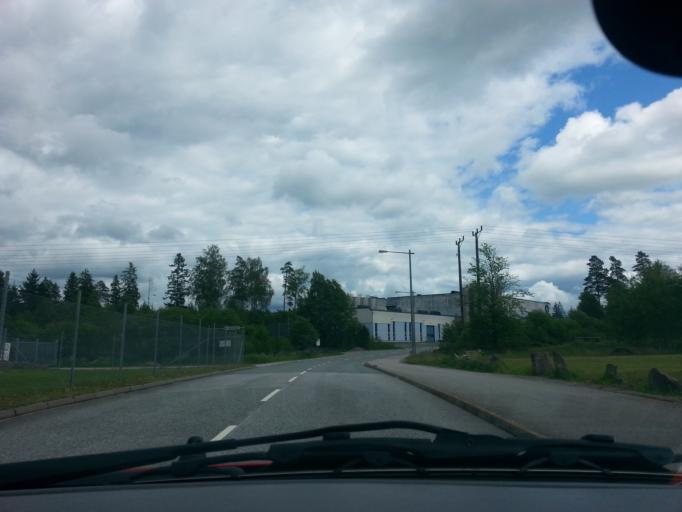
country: SE
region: Joenkoeping
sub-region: Gislaveds Kommun
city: Reftele
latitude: 57.1815
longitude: 13.5941
